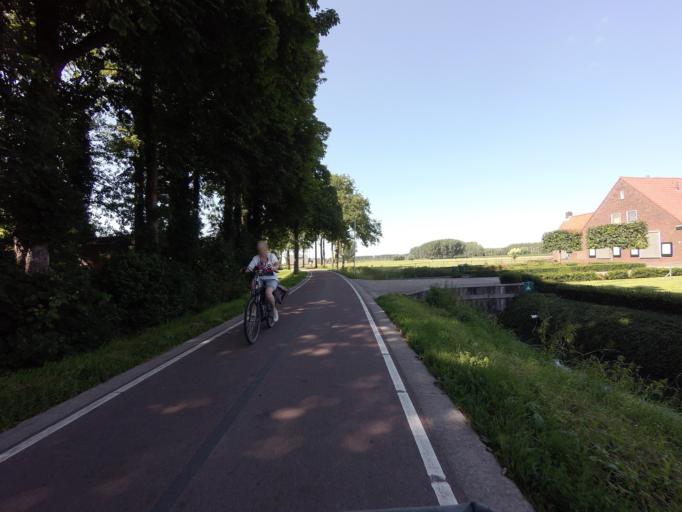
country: NL
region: Utrecht
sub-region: Gemeente Houten
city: Houten
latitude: 52.0420
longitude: 5.1565
